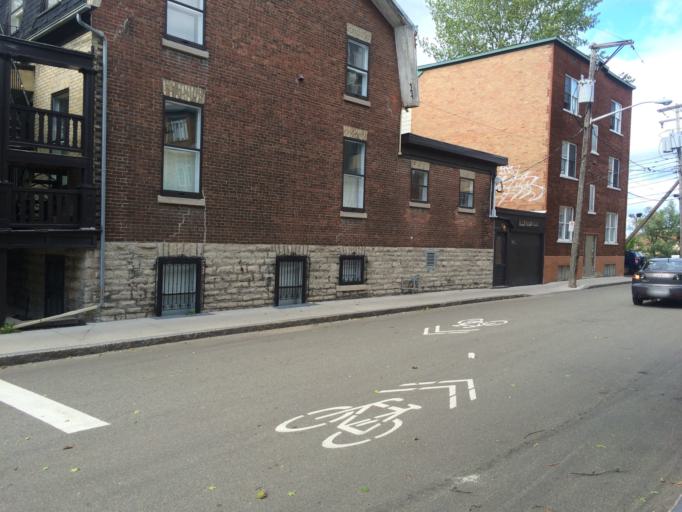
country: CA
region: Quebec
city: Quebec
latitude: 46.8036
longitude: -71.2310
